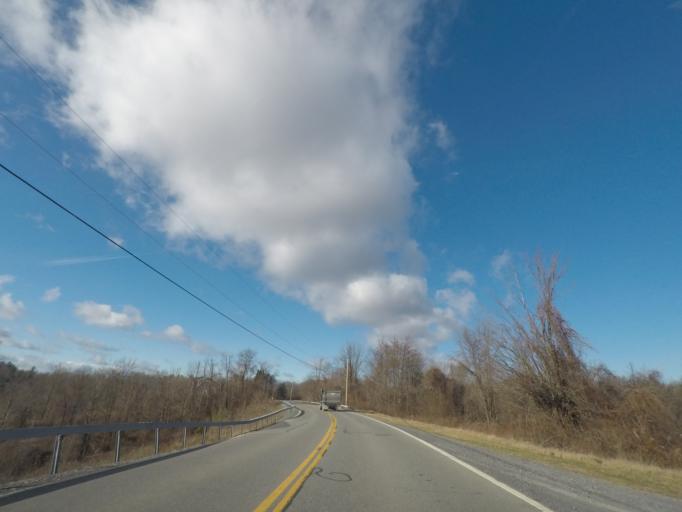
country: US
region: New York
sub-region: Saratoga County
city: Waterford
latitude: 42.8325
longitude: -73.6849
